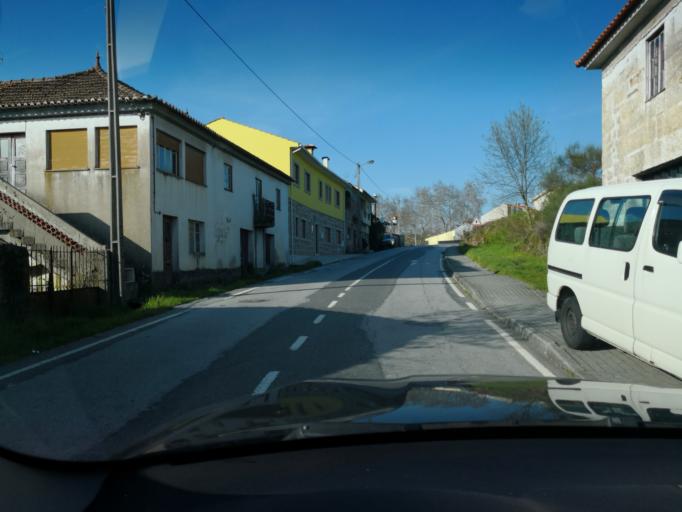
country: PT
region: Vila Real
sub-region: Vila Real
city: Vila Real
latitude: 41.3196
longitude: -7.6990
